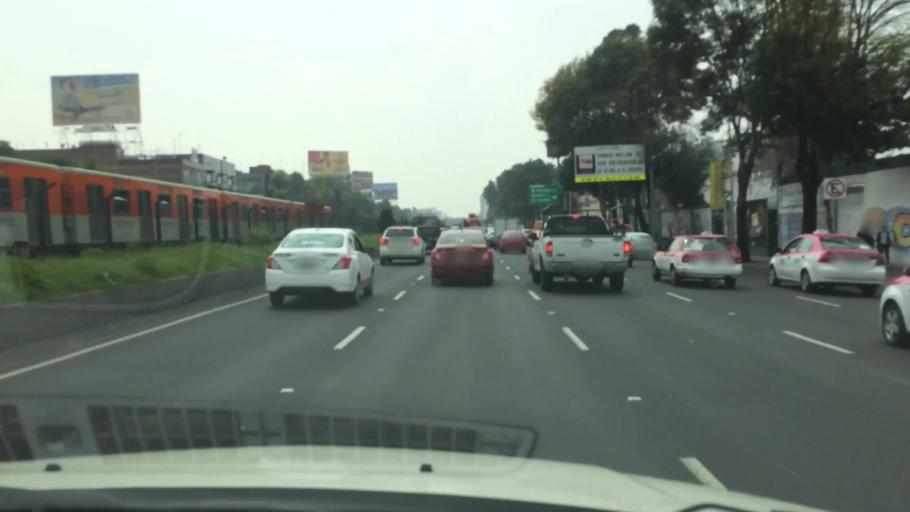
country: MX
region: Mexico City
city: Colonia Nativitas
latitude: 19.3842
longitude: -99.1396
